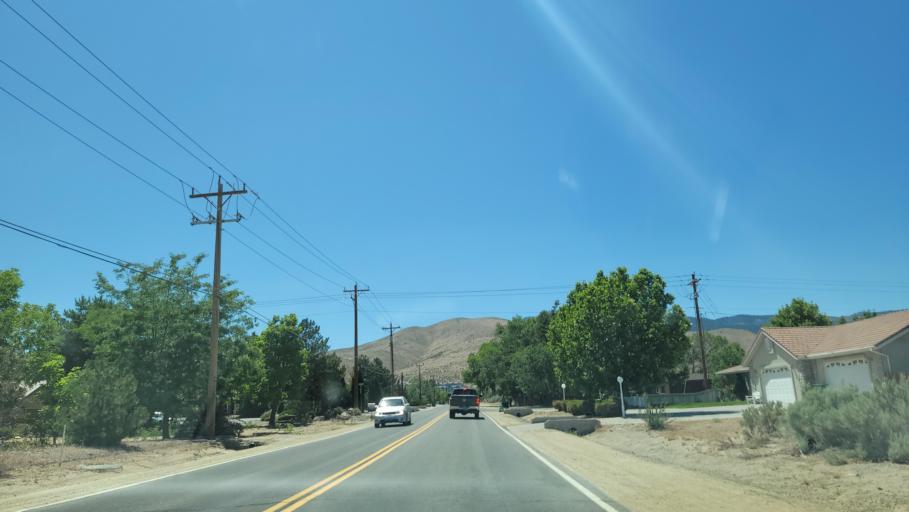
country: US
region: Nevada
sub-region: Carson City
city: Carson City
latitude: 39.1339
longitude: -119.7556
